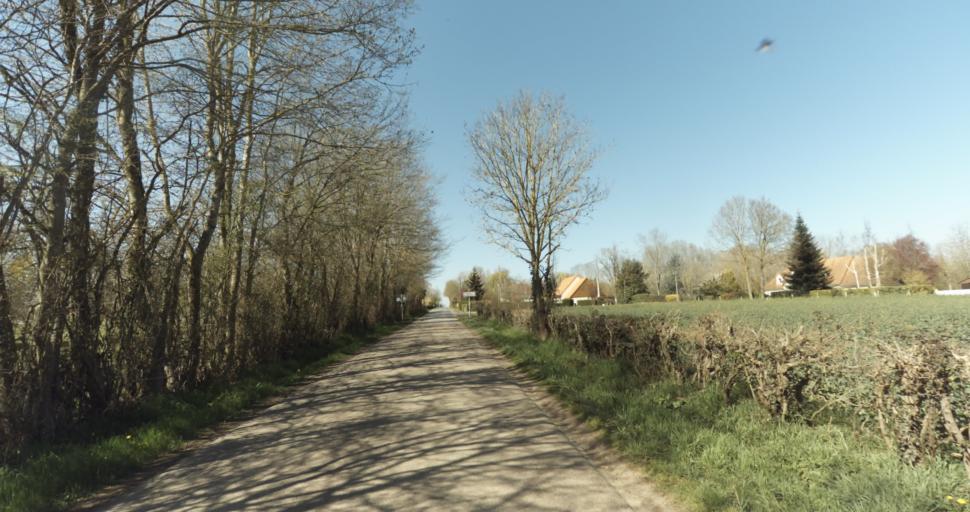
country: FR
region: Lower Normandy
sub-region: Departement du Calvados
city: Saint-Pierre-sur-Dives
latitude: 49.0029
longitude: -0.0041
